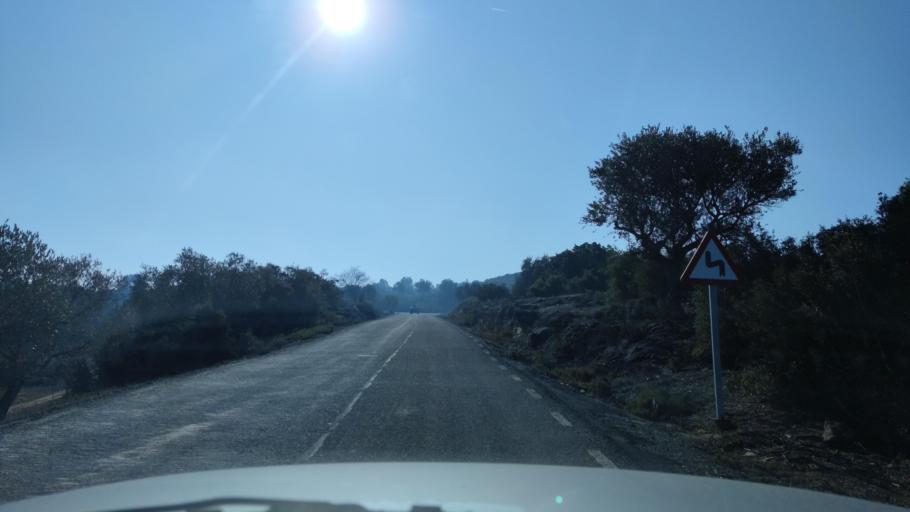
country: ES
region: Catalonia
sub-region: Provincia de Lleida
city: Torrebesses
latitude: 41.4467
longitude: 0.5585
